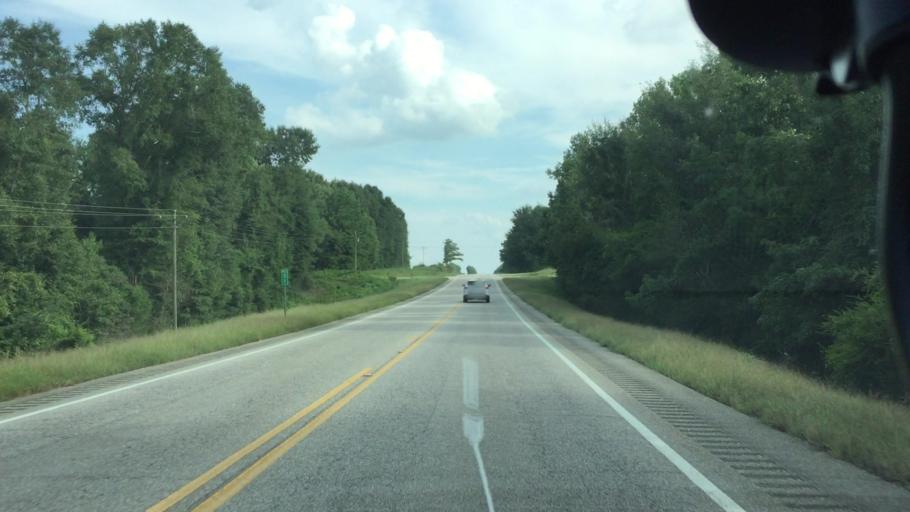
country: US
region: Alabama
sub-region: Pike County
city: Brundidge
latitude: 31.6574
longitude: -85.9518
